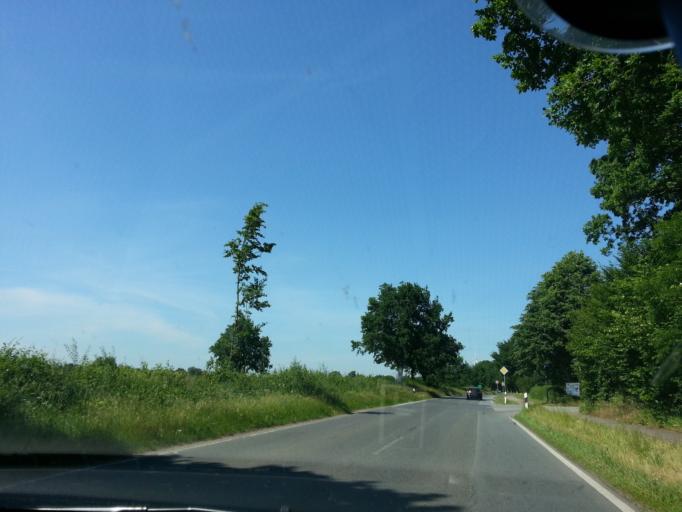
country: DE
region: Schleswig-Holstein
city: Hornbek
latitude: 53.5698
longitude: 10.6421
